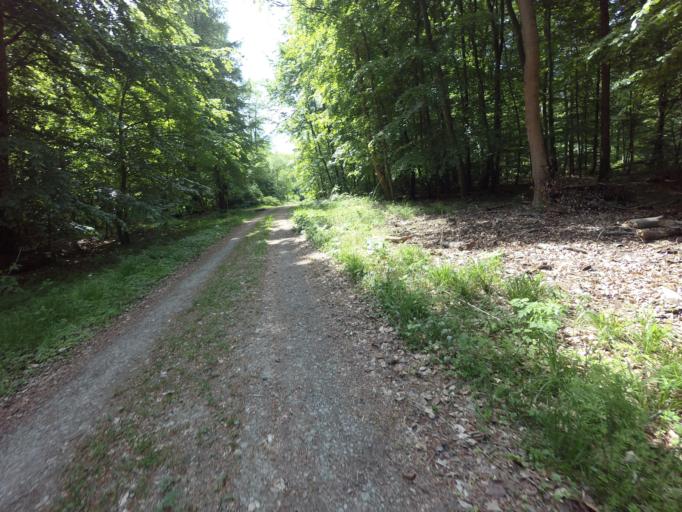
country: DE
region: Lower Saxony
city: Kneitlingen
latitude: 52.1955
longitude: 10.7583
